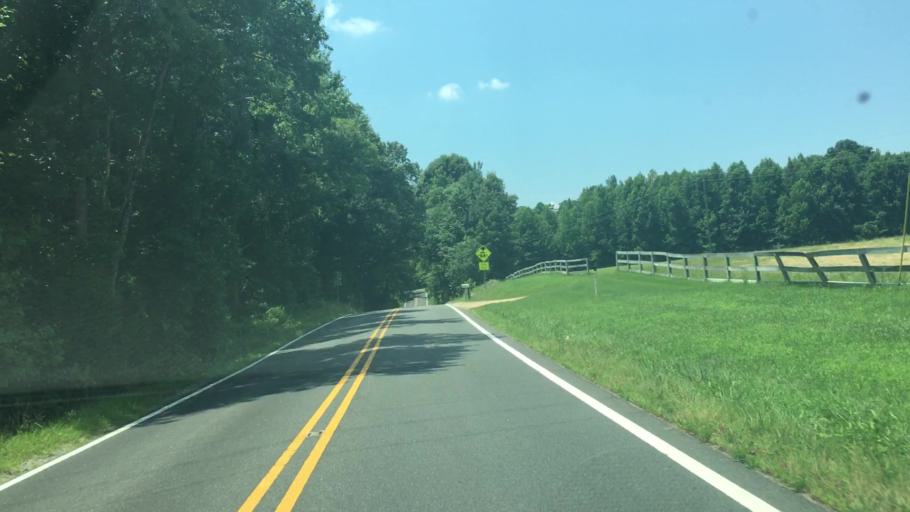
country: US
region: Virginia
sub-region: King George County
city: King George
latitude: 38.3242
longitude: -77.1741
